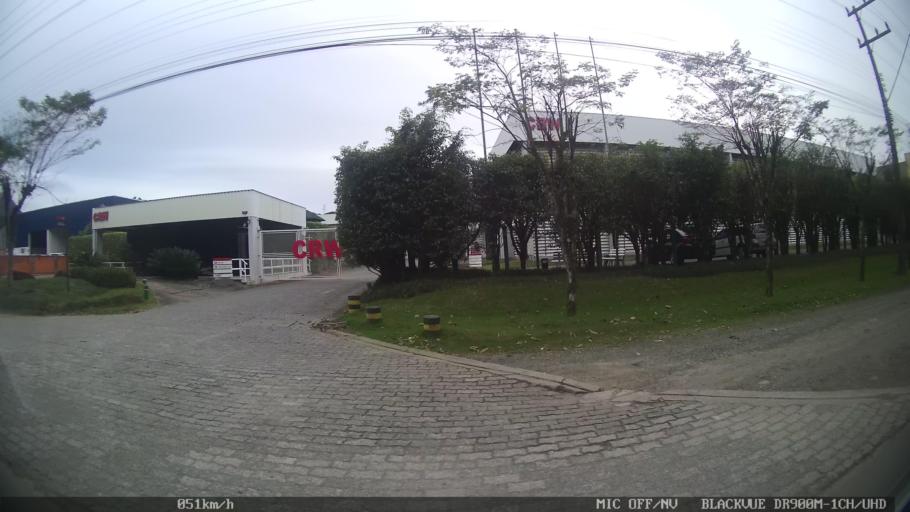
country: BR
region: Santa Catarina
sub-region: Joinville
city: Joinville
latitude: -26.2319
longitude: -48.9068
